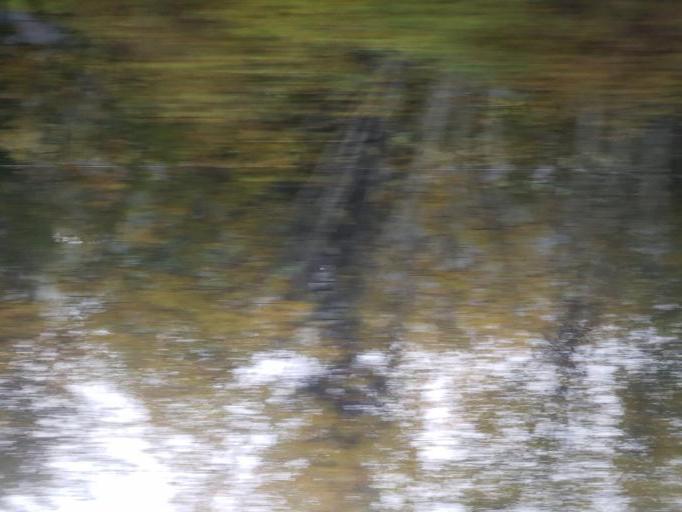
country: NO
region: Sor-Trondelag
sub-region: Trondheim
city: Trondheim
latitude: 63.3658
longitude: 10.3669
